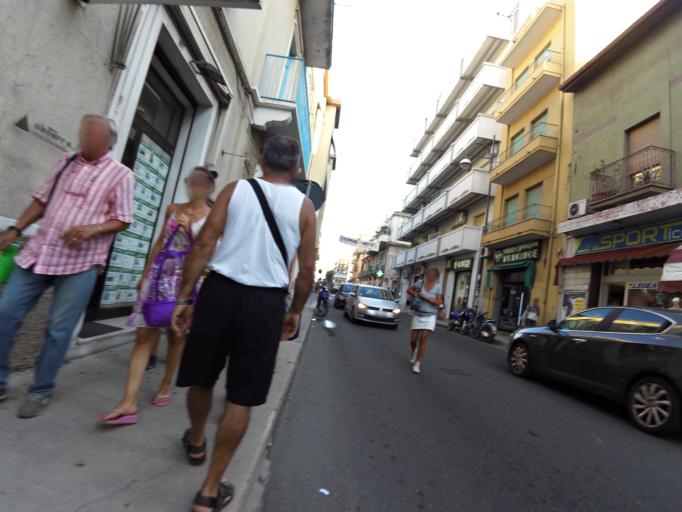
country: IT
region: Calabria
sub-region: Provincia di Catanzaro
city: Soverato Marina
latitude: 38.6888
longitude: 16.5479
